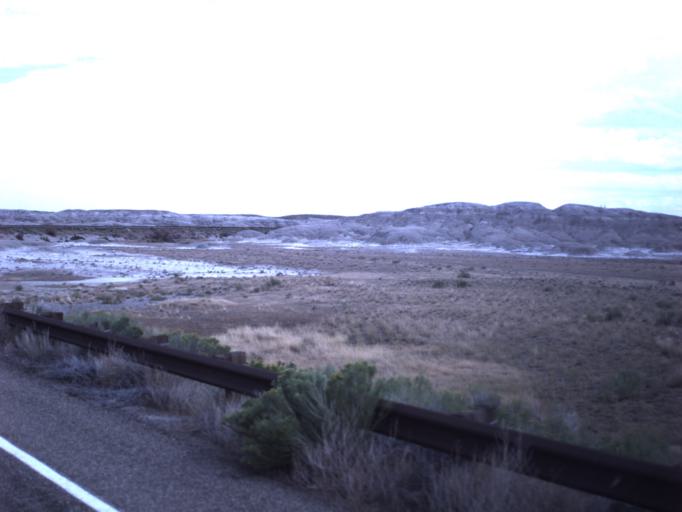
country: US
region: Utah
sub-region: Uintah County
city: Naples
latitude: 40.1095
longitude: -109.2293
